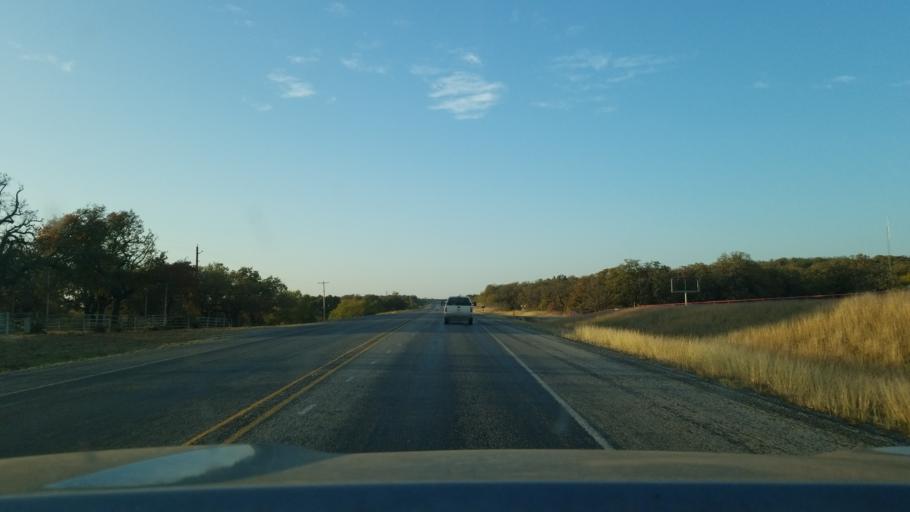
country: US
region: Texas
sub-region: Eastland County
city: Cisco
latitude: 32.3479
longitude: -98.9613
